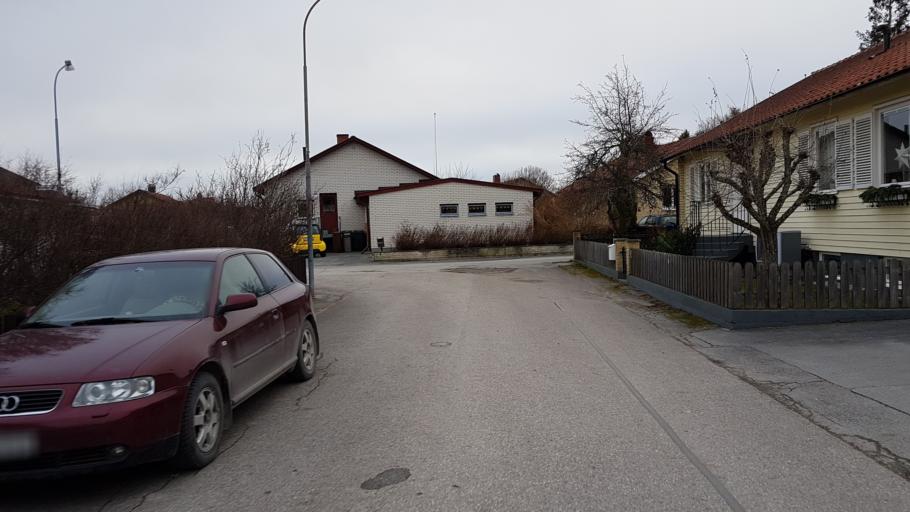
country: SE
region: Gotland
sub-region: Gotland
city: Visby
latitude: 57.6207
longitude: 18.3070
